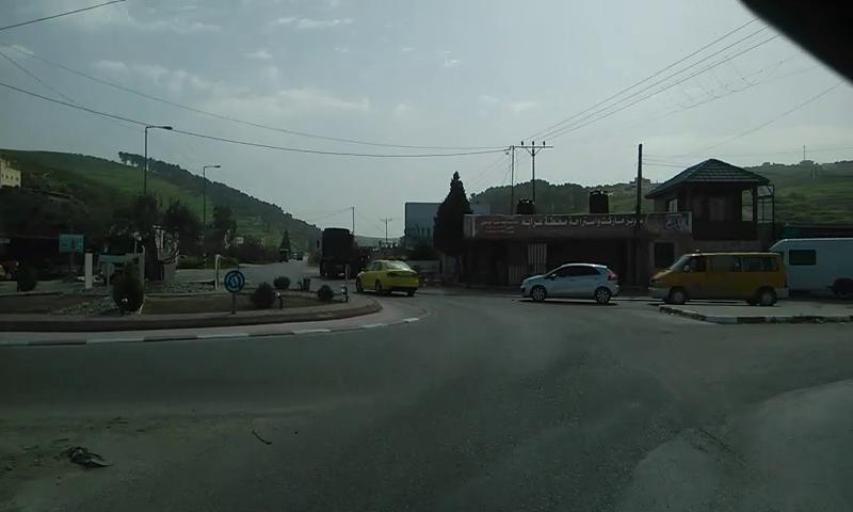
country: PS
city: Bir al Basha
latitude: 32.4080
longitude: 35.2271
